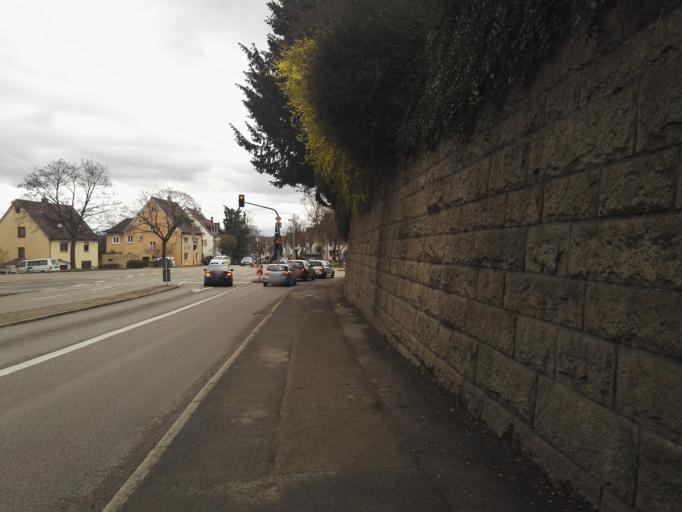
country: DE
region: Baden-Wuerttemberg
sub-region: Regierungsbezirk Stuttgart
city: Esslingen
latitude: 48.7419
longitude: 9.3274
